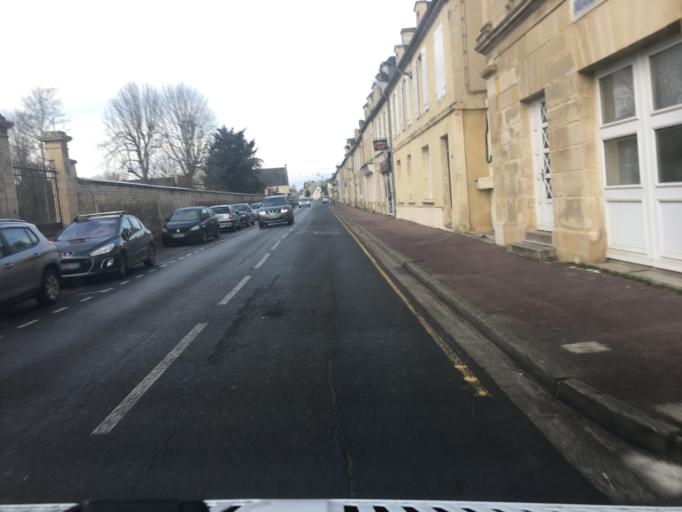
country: FR
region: Lower Normandy
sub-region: Departement du Calvados
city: Saint-Manvieu
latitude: 49.2105
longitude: -0.5122
